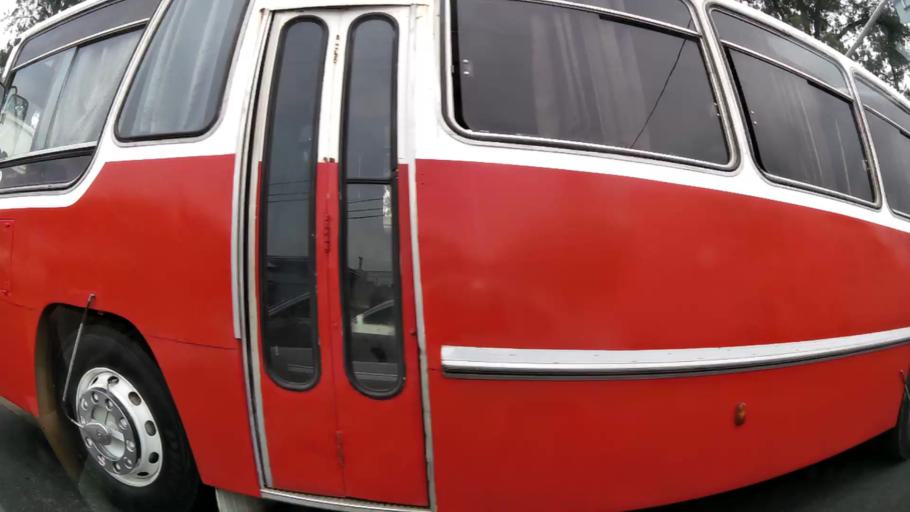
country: AR
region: Buenos Aires
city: San Justo
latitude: -34.6708
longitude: -58.5372
